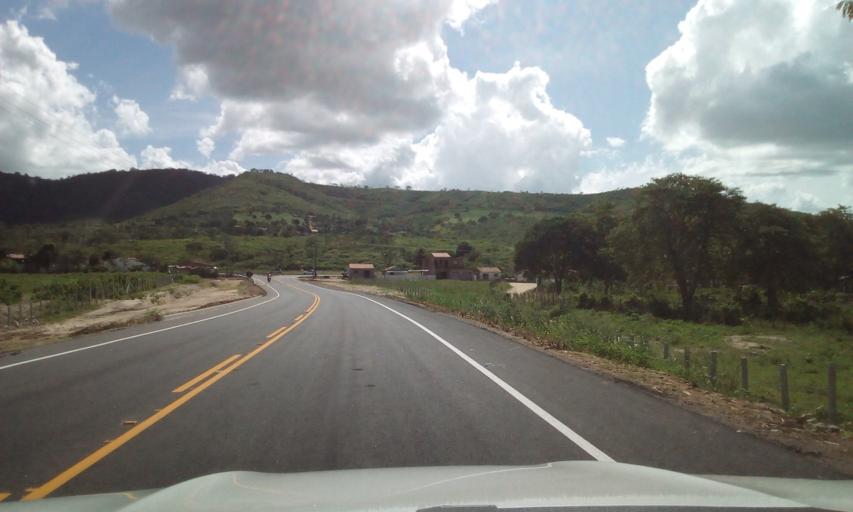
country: BR
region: Paraiba
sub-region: Guarabira
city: Guarabira
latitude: -6.8172
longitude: -35.4680
